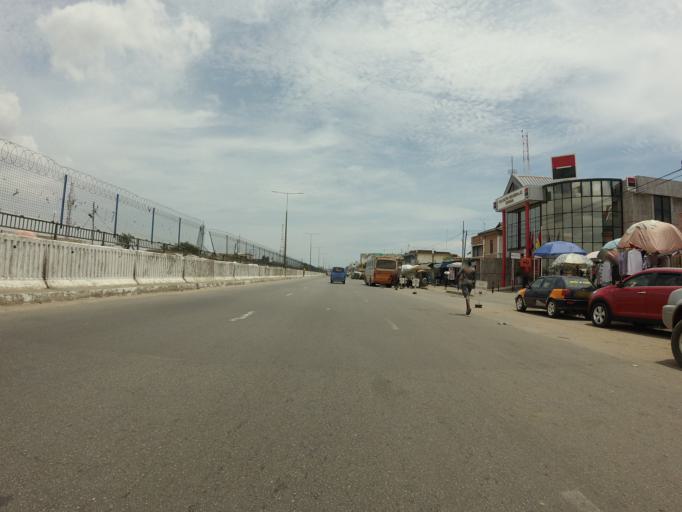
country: GH
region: Greater Accra
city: Accra
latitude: 5.5643
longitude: -0.2344
